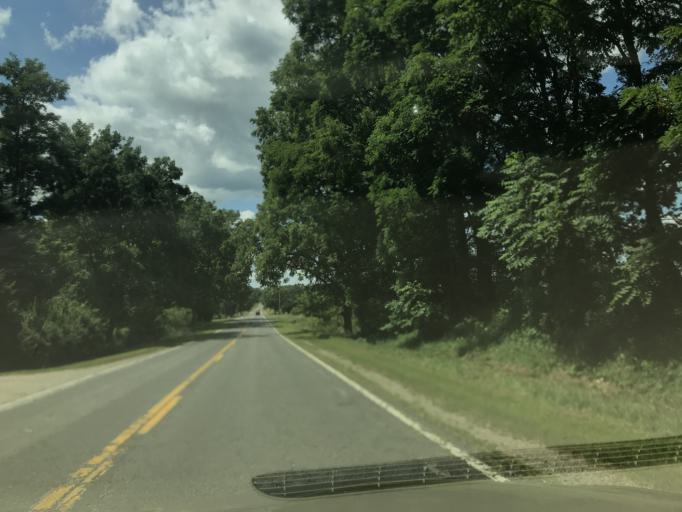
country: US
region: Michigan
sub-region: Ingham County
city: Leslie
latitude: 42.4510
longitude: -84.5345
